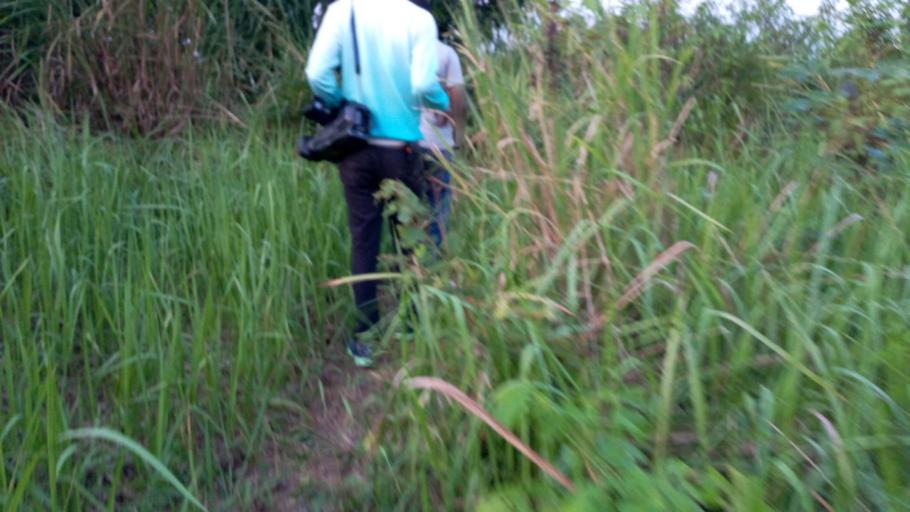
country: CD
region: Bandundu
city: Bandundu
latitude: -3.2710
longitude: 17.3843
